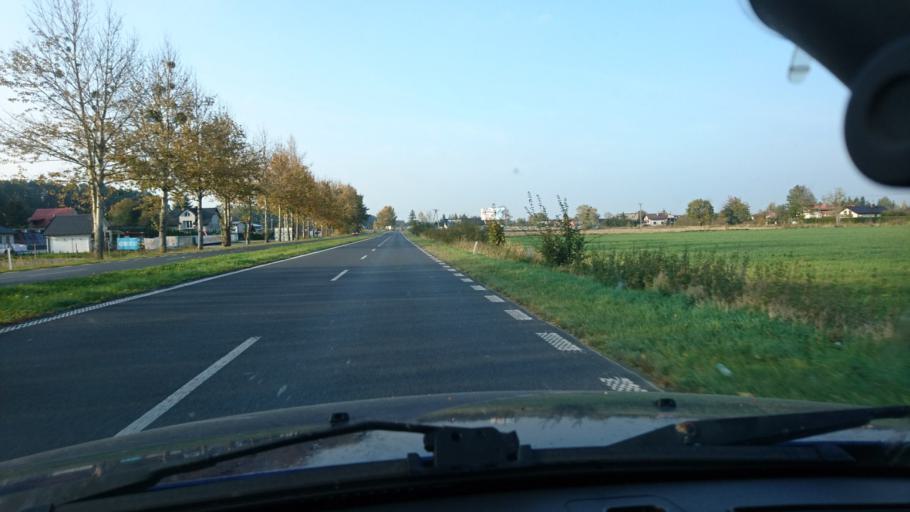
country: PL
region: Silesian Voivodeship
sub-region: Powiat cieszynski
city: Ustron
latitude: 49.7324
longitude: 18.7929
